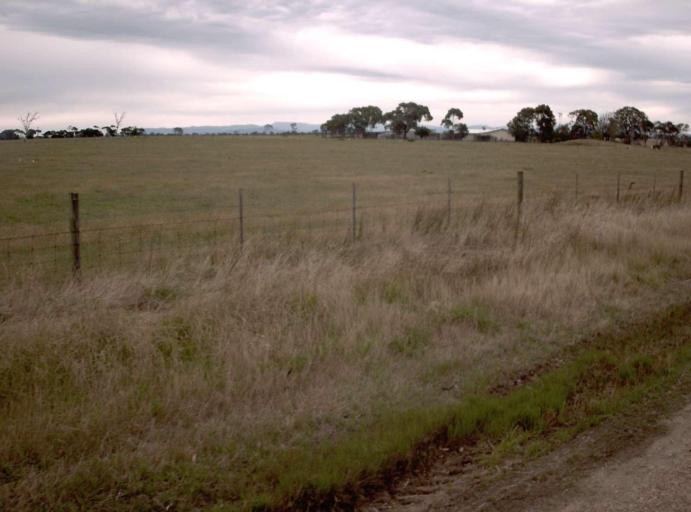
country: AU
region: Victoria
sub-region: Wellington
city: Sale
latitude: -37.9978
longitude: 147.1918
